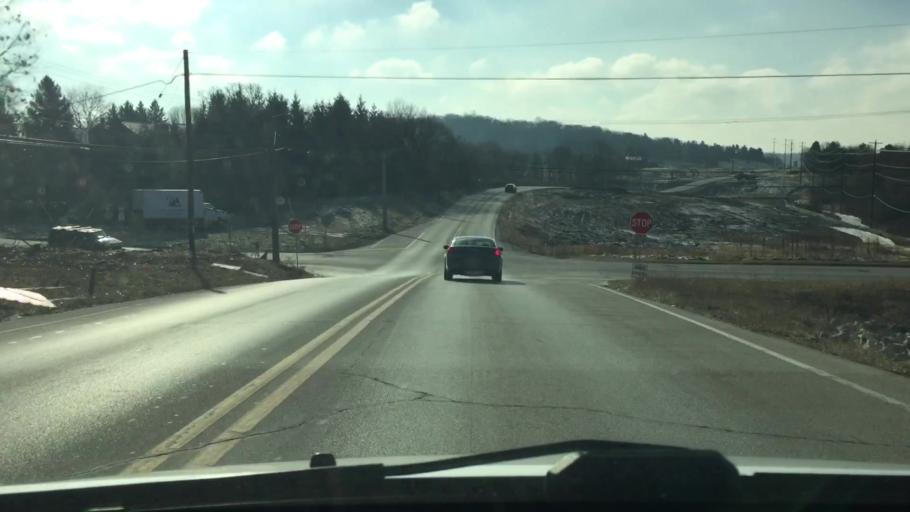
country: US
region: Wisconsin
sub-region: Waukesha County
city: Waukesha
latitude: 43.0136
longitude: -88.2860
